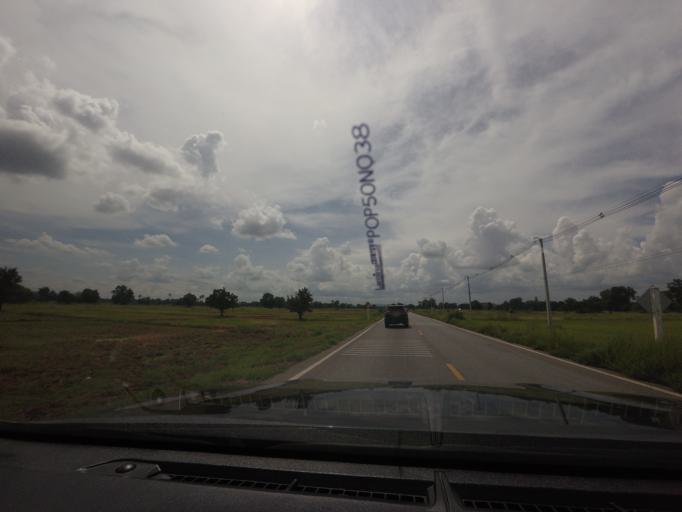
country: TH
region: Kanchanaburi
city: Phanom Thuan
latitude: 14.1761
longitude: 99.5960
